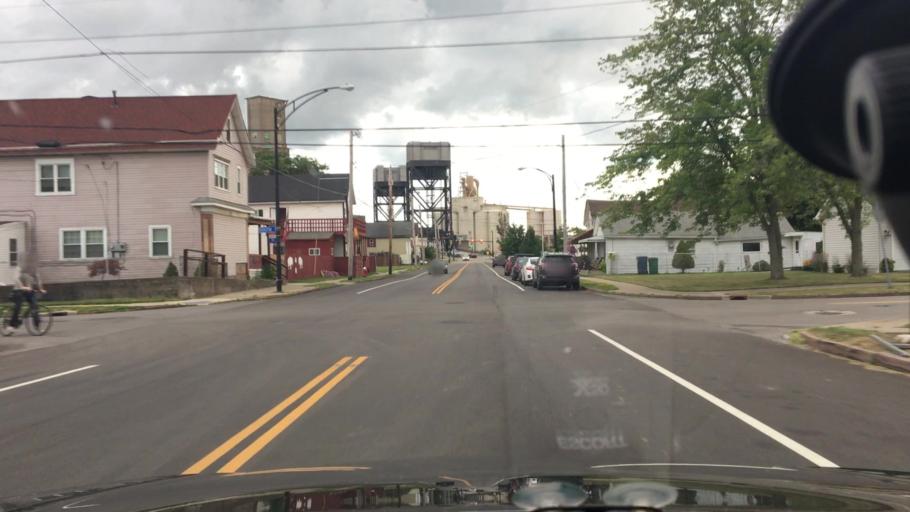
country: US
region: New York
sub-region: Erie County
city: Buffalo
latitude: 42.8654
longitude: -78.8667
